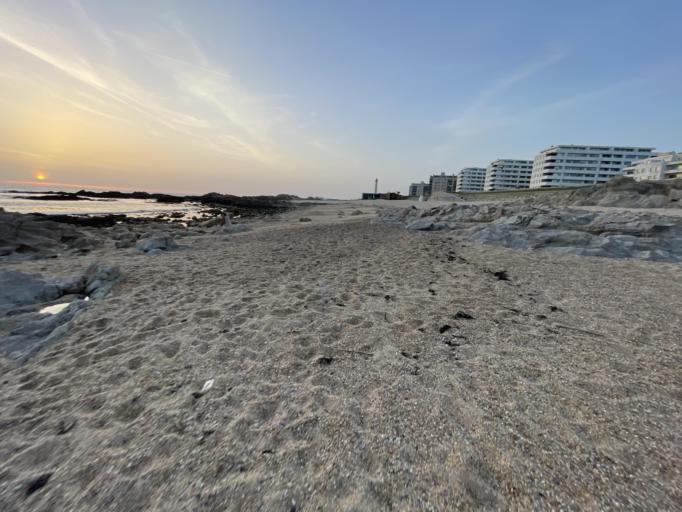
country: PT
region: Porto
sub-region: Matosinhos
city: Leca da Palmeira
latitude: 41.1957
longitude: -8.7098
